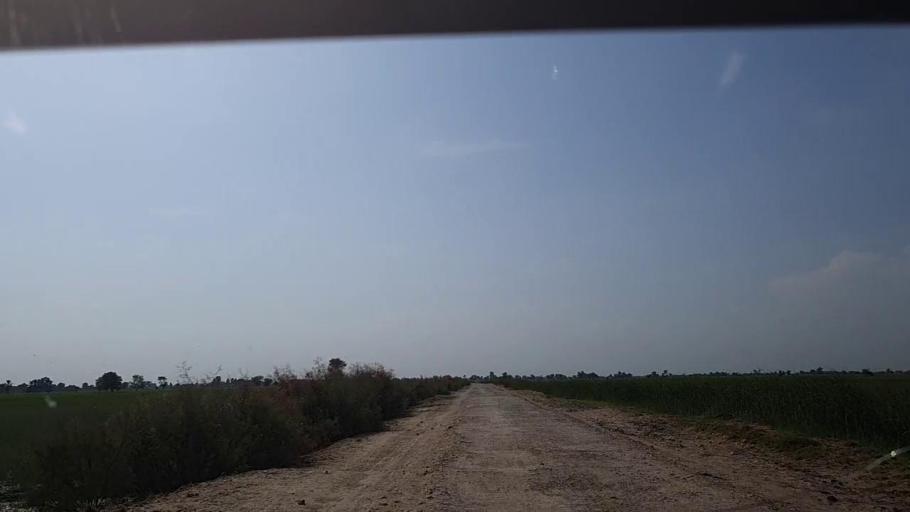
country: PK
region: Sindh
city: Khanpur
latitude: 27.8498
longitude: 69.3666
